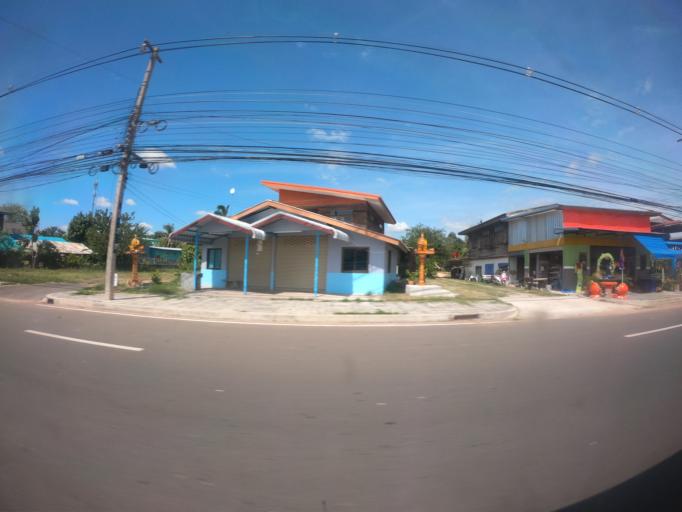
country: TH
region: Surin
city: Prasat
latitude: 14.6178
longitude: 103.4146
